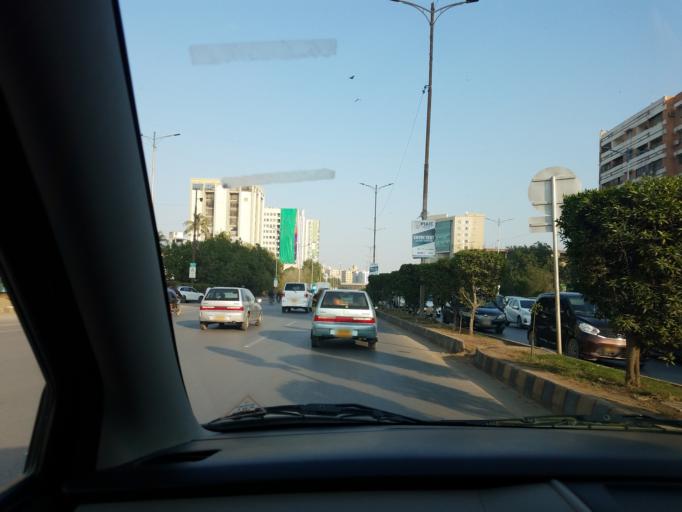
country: PK
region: Sindh
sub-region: Karachi District
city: Karachi
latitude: 24.8598
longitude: 67.0544
